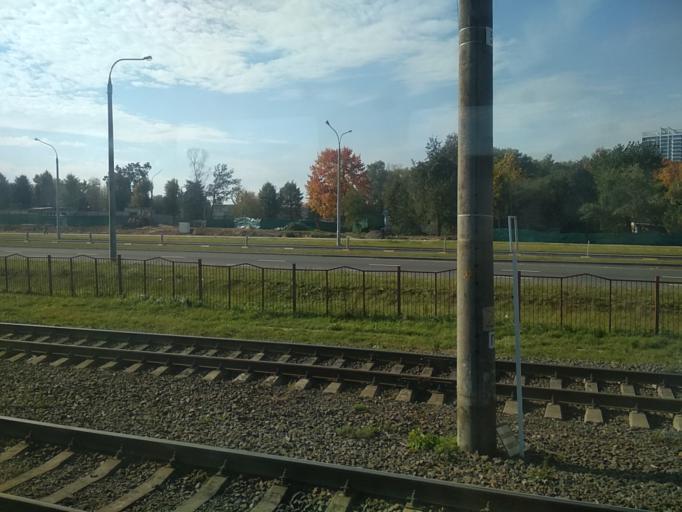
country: BY
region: Minsk
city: Minsk
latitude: 53.8681
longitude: 27.5611
